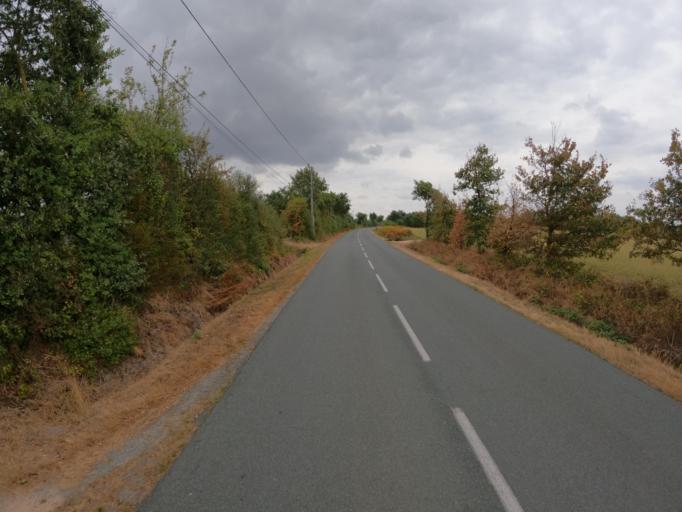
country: FR
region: Pays de la Loire
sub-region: Departement de la Vendee
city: Tiffauges
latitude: 47.0033
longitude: -1.0971
